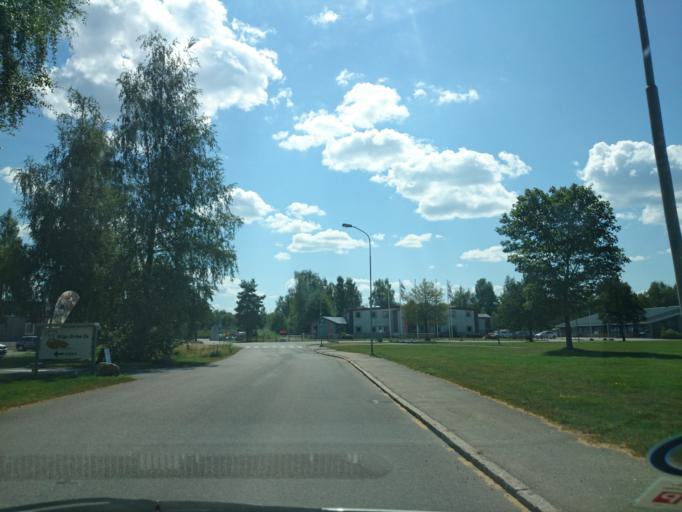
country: SE
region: Joenkoeping
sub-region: Varnamo Kommun
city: Varnamo
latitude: 57.1763
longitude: 14.0579
